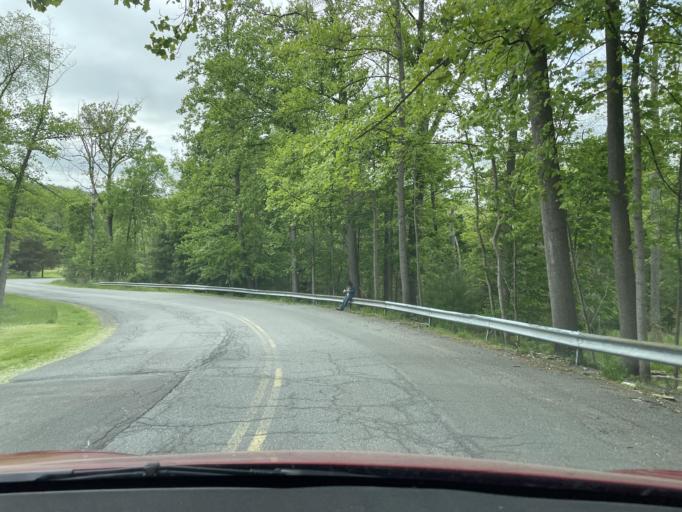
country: US
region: New York
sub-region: Ulster County
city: Woodstock
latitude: 42.0265
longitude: -74.1013
